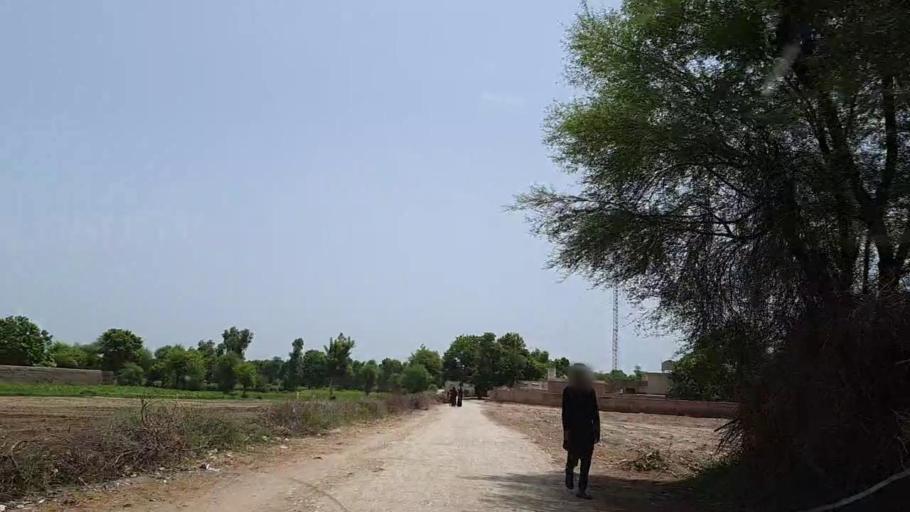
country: PK
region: Sindh
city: Tharu Shah
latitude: 26.9689
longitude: 68.0398
